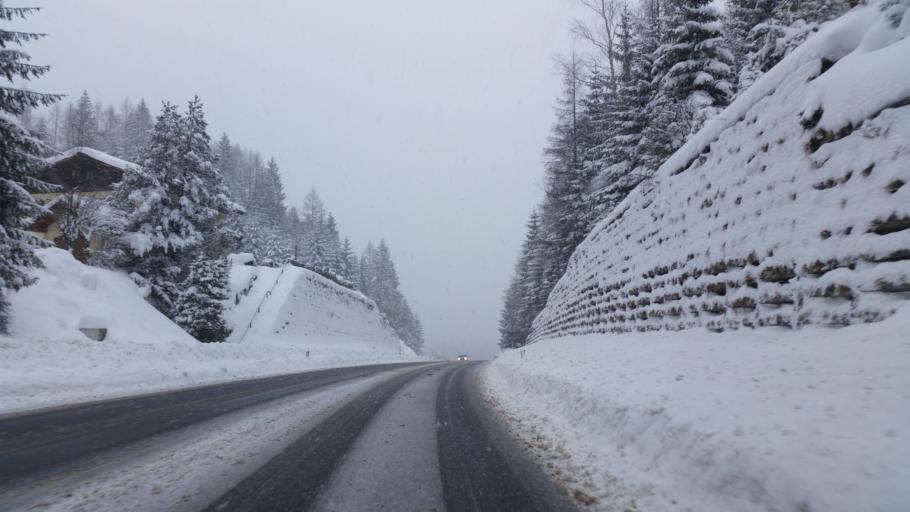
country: AT
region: Salzburg
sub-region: Politischer Bezirk Hallein
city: Scheffau am Tennengebirge
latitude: 47.5840
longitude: 13.2700
